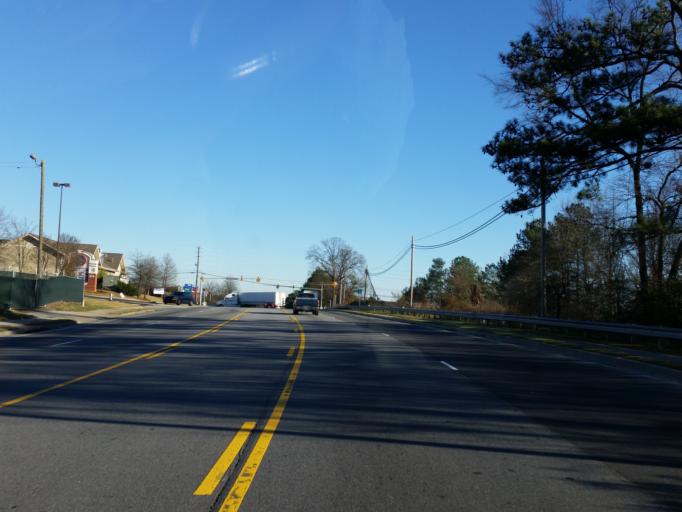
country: US
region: Georgia
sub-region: Cobb County
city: Vinings
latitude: 33.8384
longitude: -84.4827
